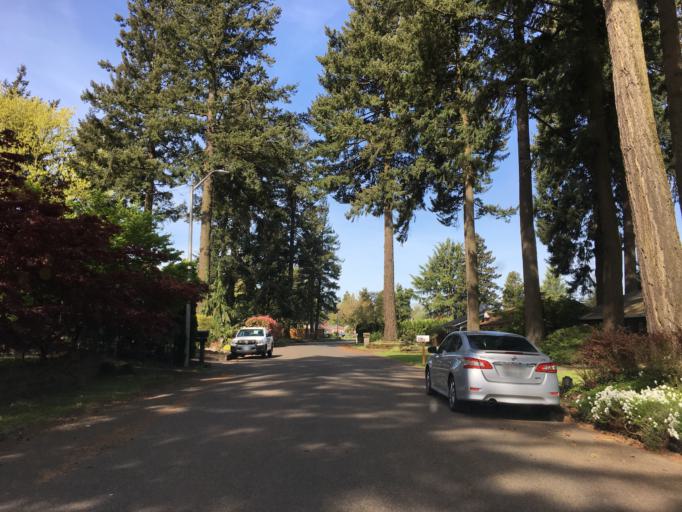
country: US
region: Oregon
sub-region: Multnomah County
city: Lents
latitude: 45.5365
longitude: -122.5276
